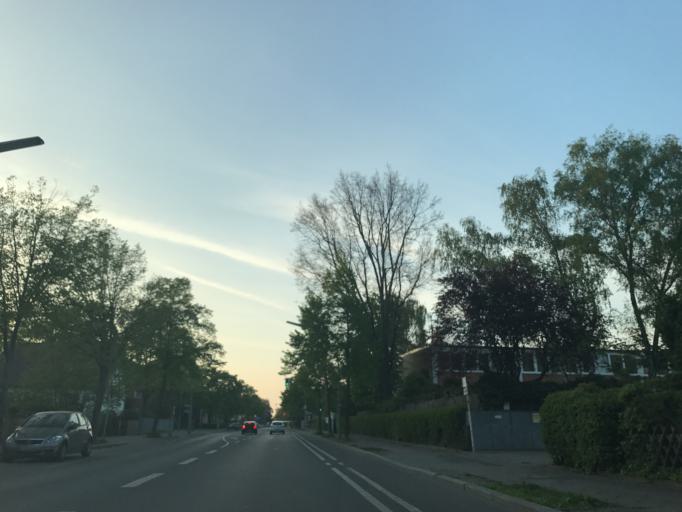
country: DE
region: Berlin
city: Staaken
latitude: 52.5306
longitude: 13.1590
